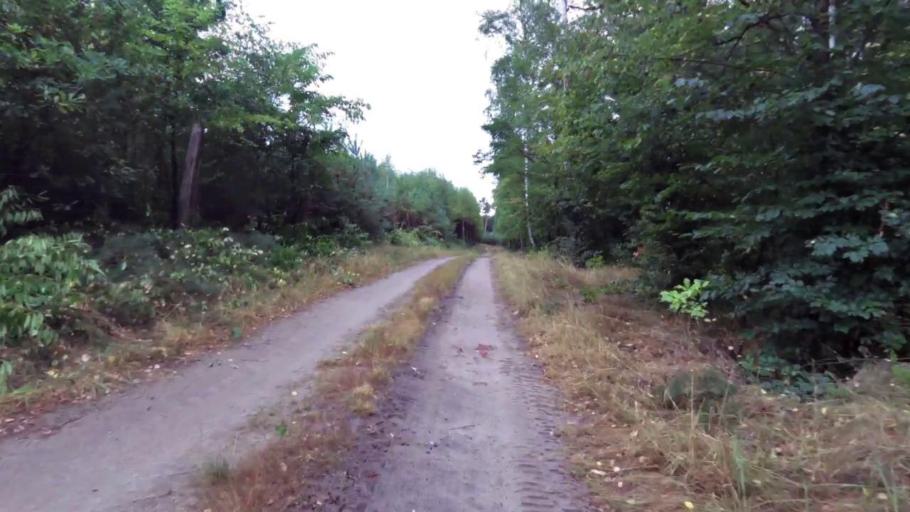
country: PL
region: West Pomeranian Voivodeship
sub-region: Powiat mysliborski
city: Debno
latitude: 52.8315
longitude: 14.6727
